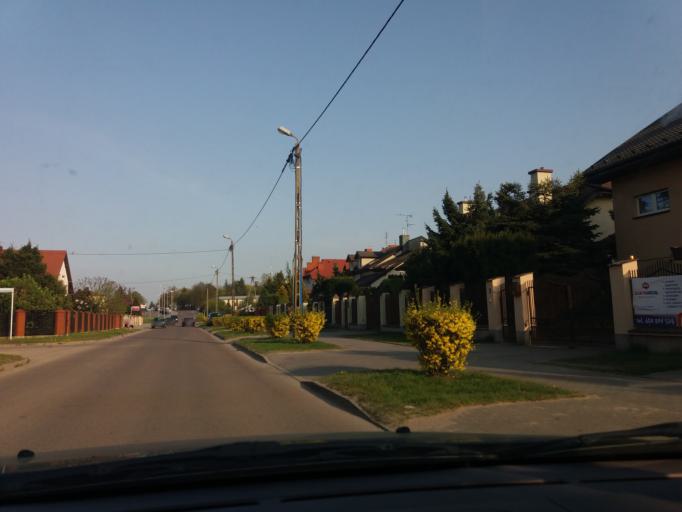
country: PL
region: Masovian Voivodeship
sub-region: Powiat mlawski
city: Mlawa
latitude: 53.1248
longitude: 20.3669
